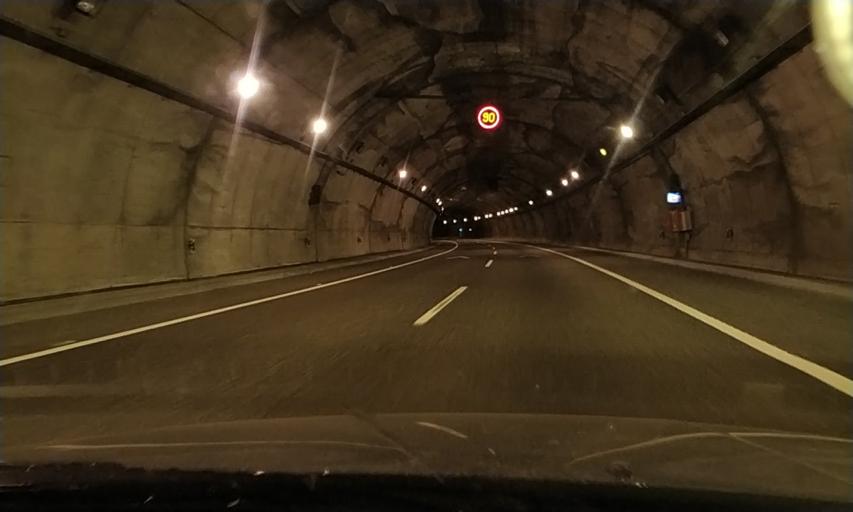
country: ES
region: Galicia
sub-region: Provincia de Lugo
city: Becerrea
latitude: 42.7879
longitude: -7.1096
